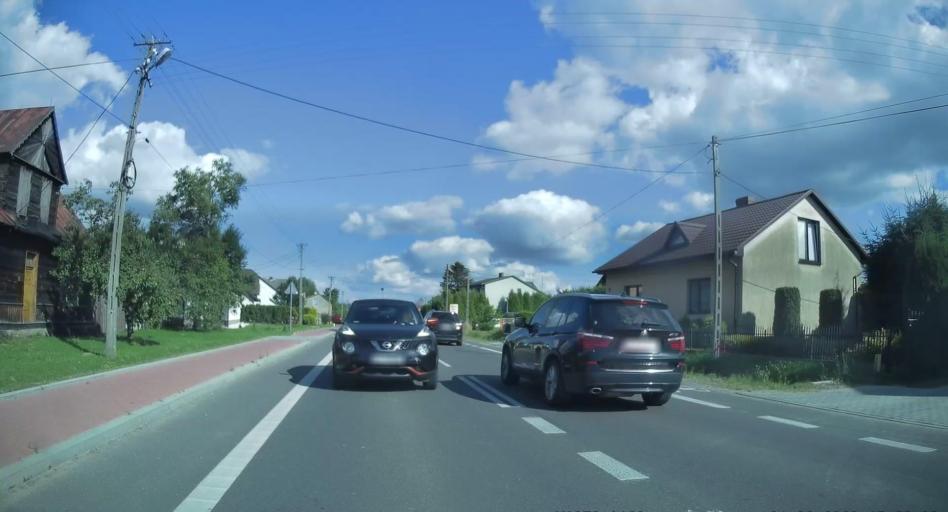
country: PL
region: Swietokrzyskie
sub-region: Powiat kielecki
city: Bodzentyn
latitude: 50.9337
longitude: 20.9668
